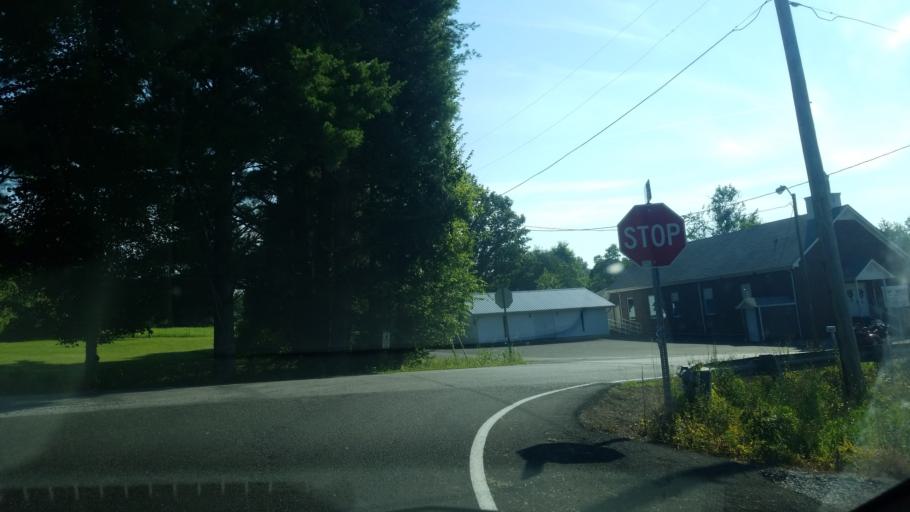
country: US
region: Tennessee
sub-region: Loudon County
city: Loudon
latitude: 35.8061
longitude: -84.3608
